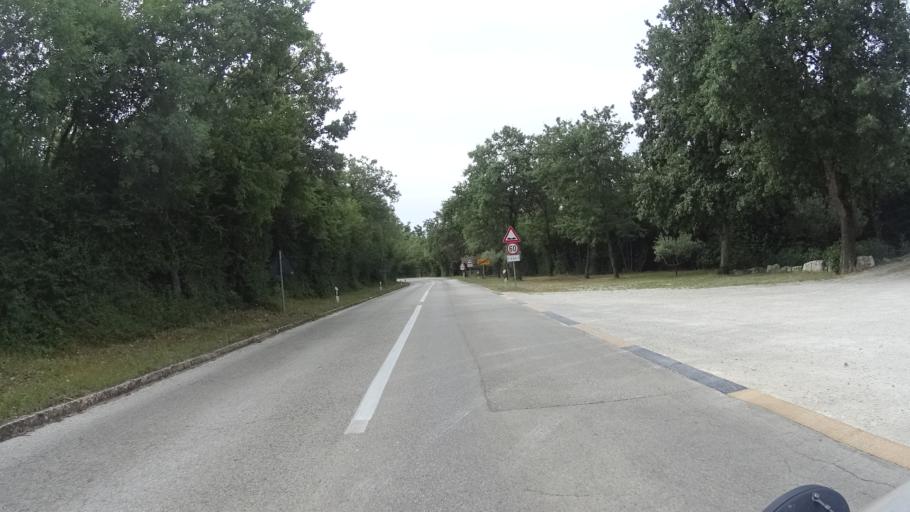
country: HR
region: Istarska
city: Vrsar
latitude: 45.1584
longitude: 13.6911
